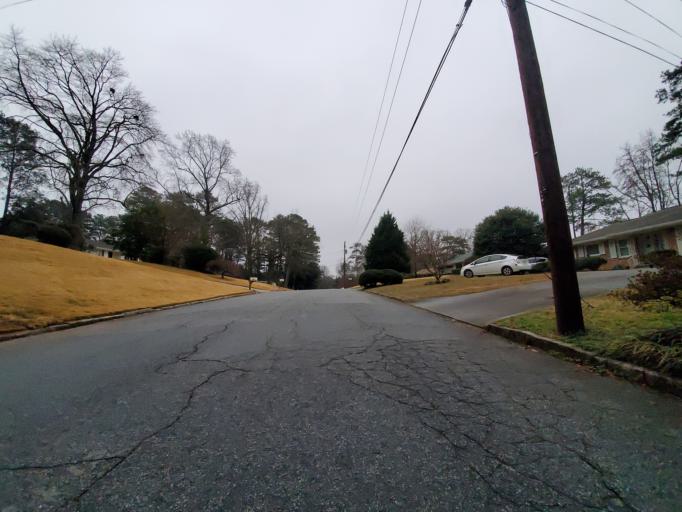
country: US
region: Georgia
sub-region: DeKalb County
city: North Decatur
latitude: 33.7983
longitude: -84.3029
